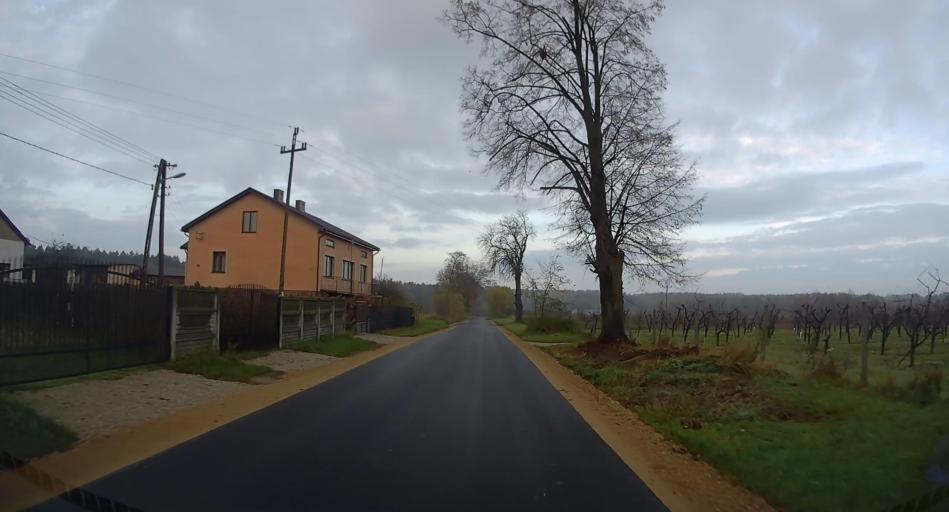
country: PL
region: Lodz Voivodeship
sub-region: Powiat skierniewicki
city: Kowiesy
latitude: 51.9277
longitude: 20.4024
